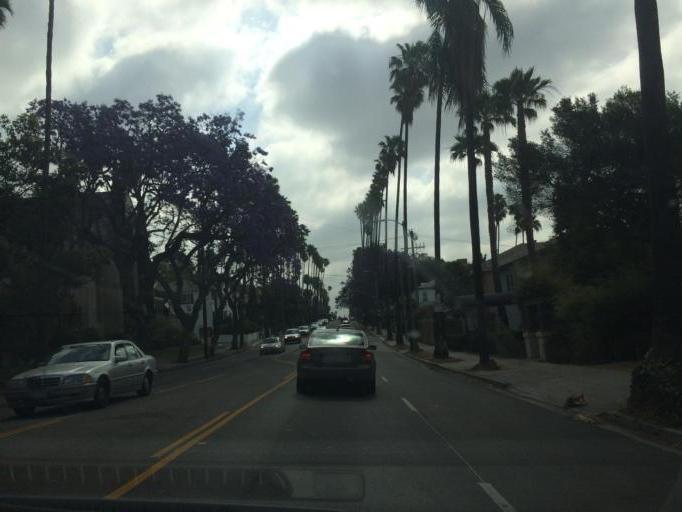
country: US
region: California
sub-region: Los Angeles County
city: West Hollywood
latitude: 34.1017
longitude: -118.3538
